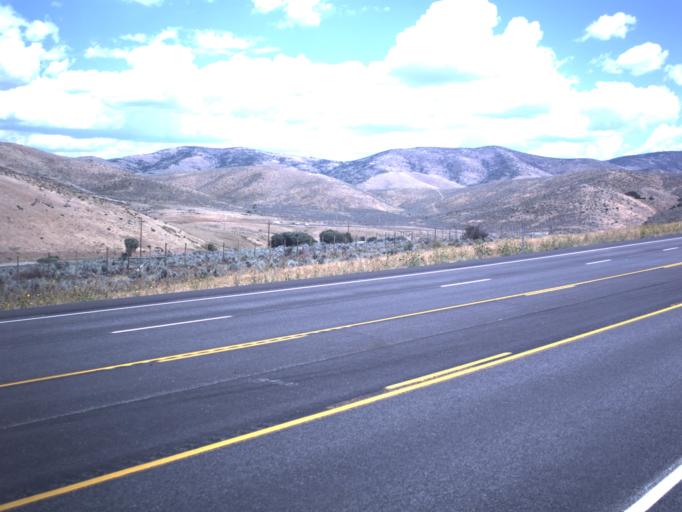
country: US
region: Utah
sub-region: Wasatch County
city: Midway
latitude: 40.4063
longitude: -111.4906
